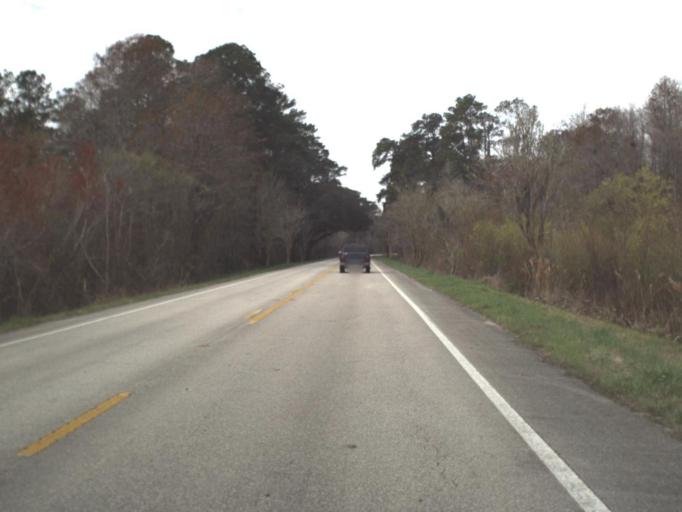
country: US
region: Florida
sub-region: Jefferson County
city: Monticello
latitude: 30.5297
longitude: -83.9688
